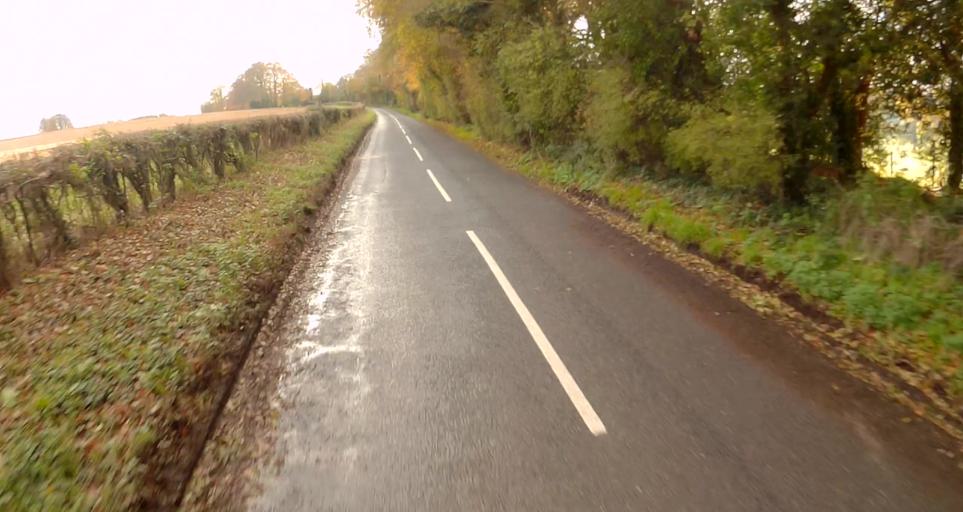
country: GB
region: England
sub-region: Hampshire
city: Old Basing
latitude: 51.2434
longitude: -1.0397
